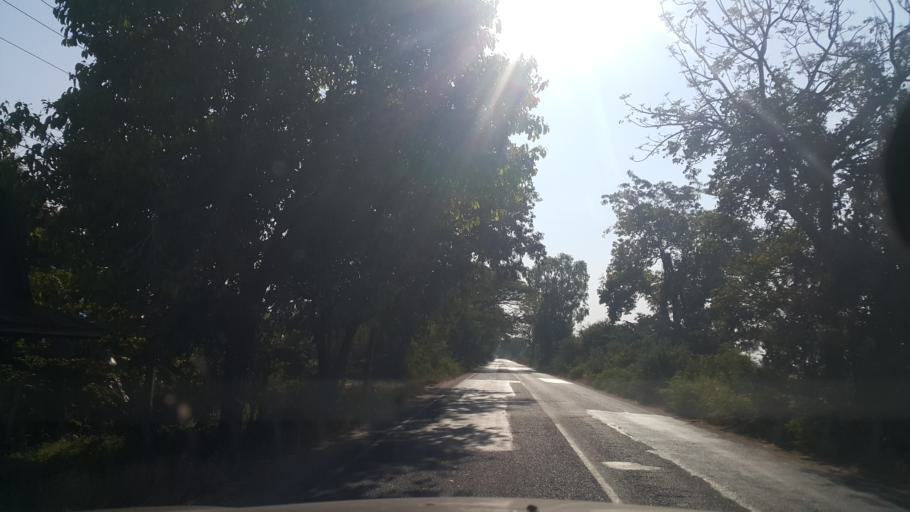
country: TH
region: Nakhon Ratchasima
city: Phimai
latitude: 15.2064
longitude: 102.4415
